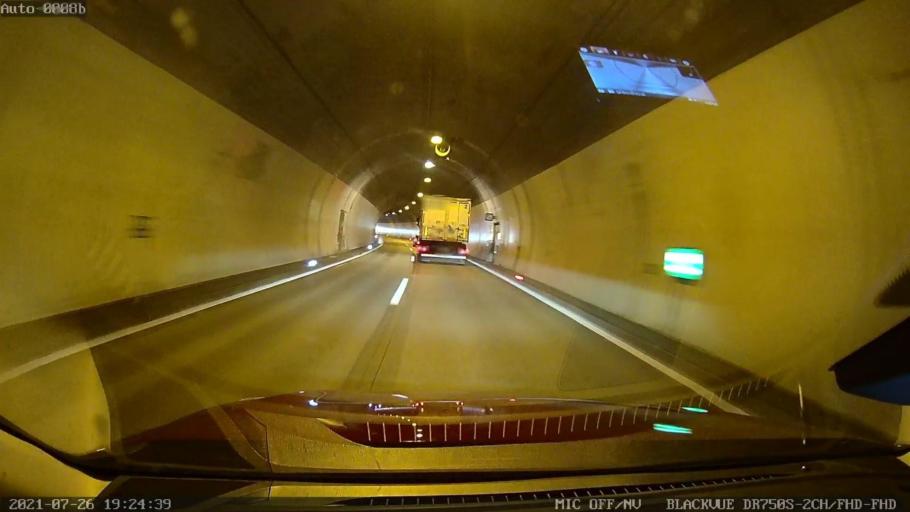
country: AT
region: Upper Austria
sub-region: Politischer Bezirk Kirchdorf an der Krems
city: Micheldorf in Oberoesterreich
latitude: 47.8670
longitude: 14.1321
